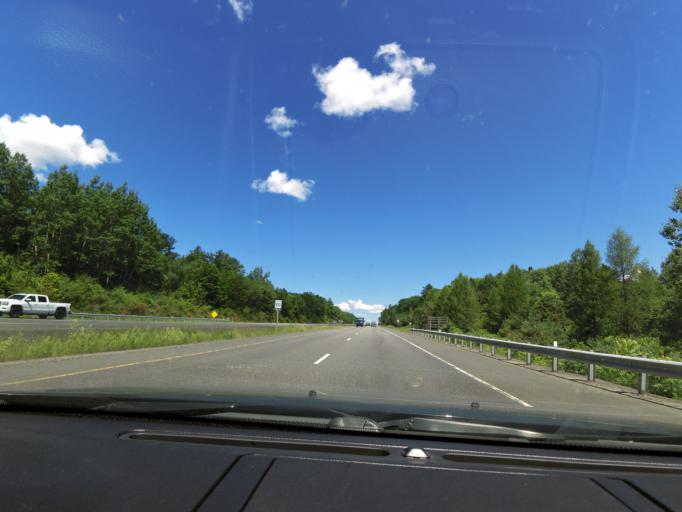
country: CA
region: Ontario
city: Bracebridge
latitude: 45.0927
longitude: -79.3025
